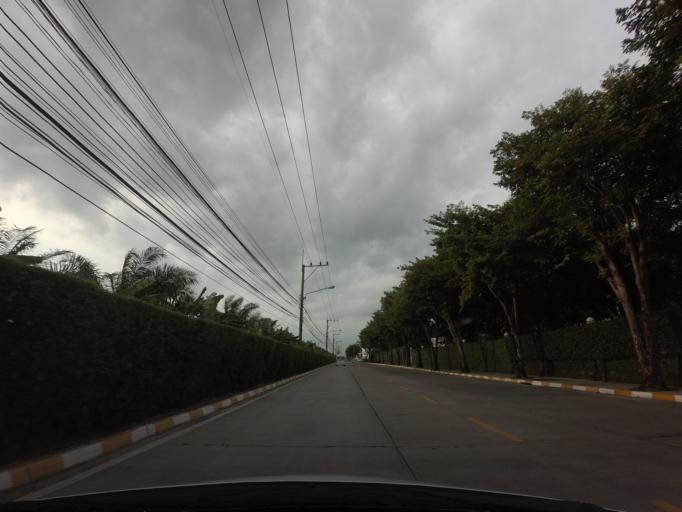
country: TH
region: Pathum Thani
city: Thanyaburi
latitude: 13.9898
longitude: 100.6745
